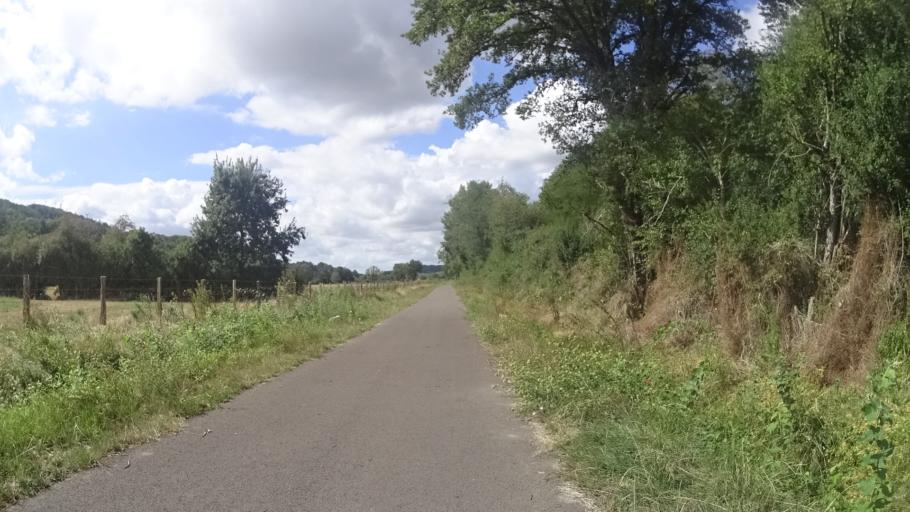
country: FR
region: Bourgogne
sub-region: Departement de Saone-et-Loire
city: Ecuisses
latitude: 46.8055
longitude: 4.5730
